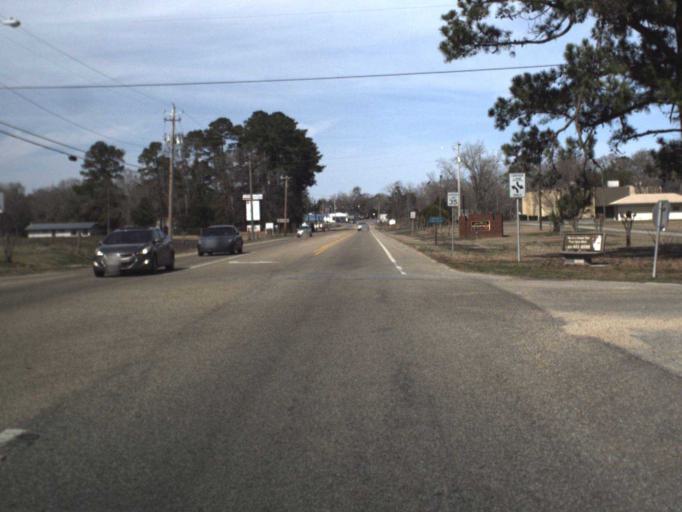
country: US
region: Florida
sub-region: Jackson County
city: Graceville
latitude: 30.9461
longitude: -85.5153
